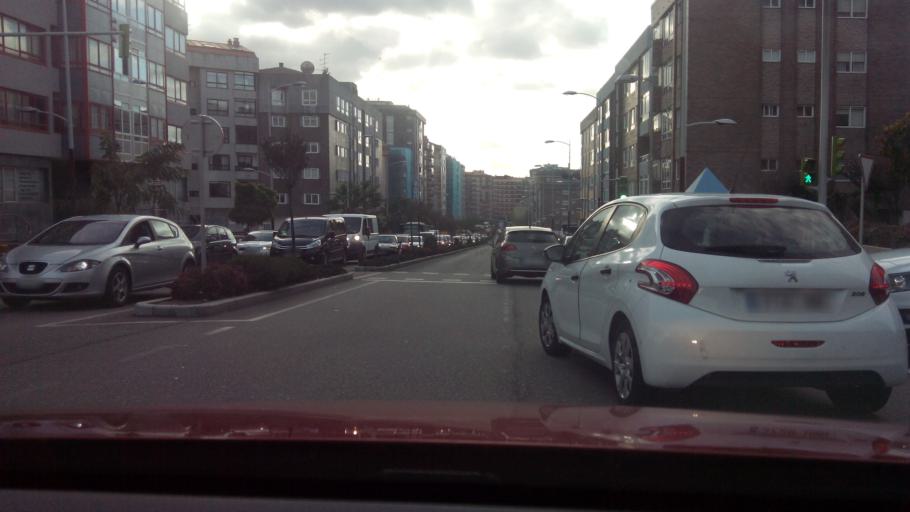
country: ES
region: Galicia
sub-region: Provincia de Pontevedra
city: Vigo
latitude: 42.2269
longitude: -8.7020
